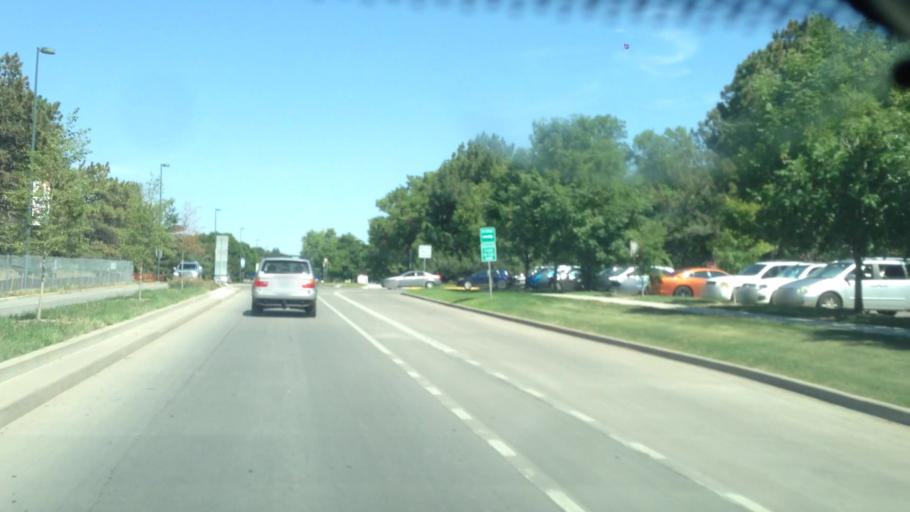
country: US
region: Colorado
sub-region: Denver County
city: Denver
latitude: 39.7512
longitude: -104.9466
